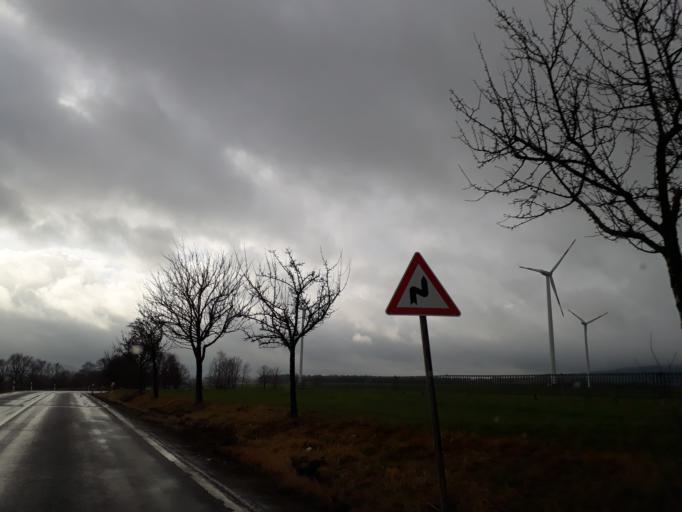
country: DE
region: Saxony
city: Herrnhut
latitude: 51.0122
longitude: 14.7313
